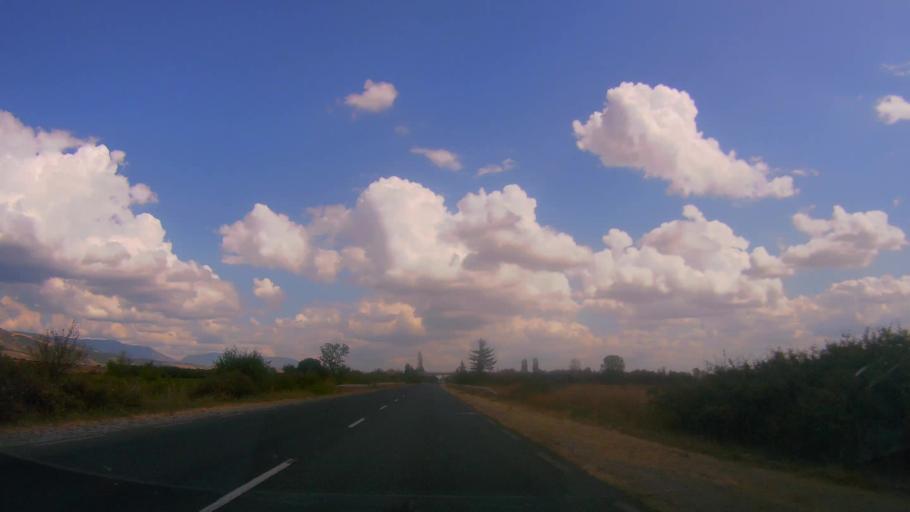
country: BG
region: Sliven
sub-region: Obshtina Sliven
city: Sliven
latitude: 42.6364
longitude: 26.2284
